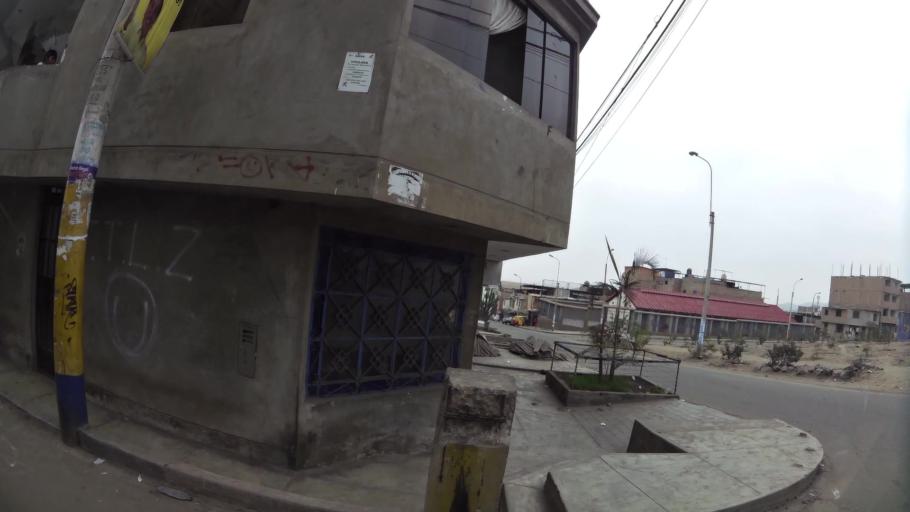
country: PE
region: Lima
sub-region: Lima
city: Surco
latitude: -12.1741
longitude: -76.9613
